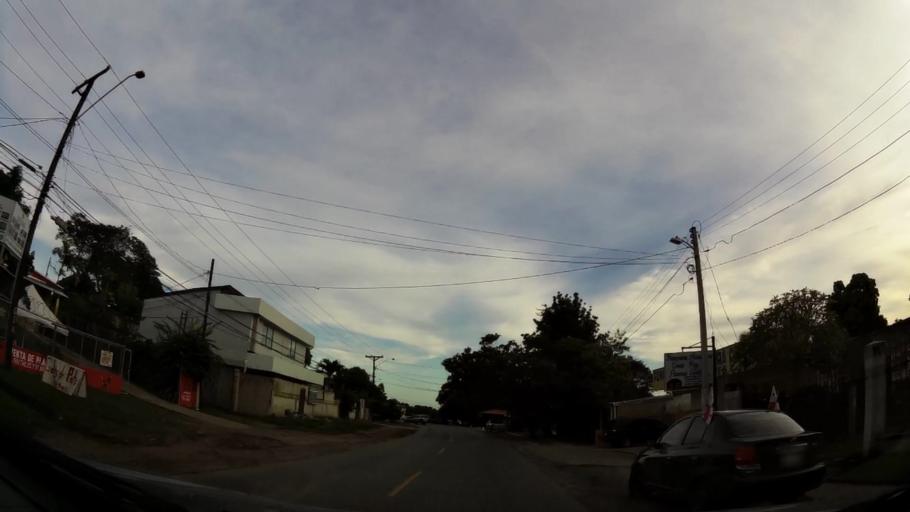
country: PA
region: Panama
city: La Chorrera
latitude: 8.8749
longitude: -79.7783
